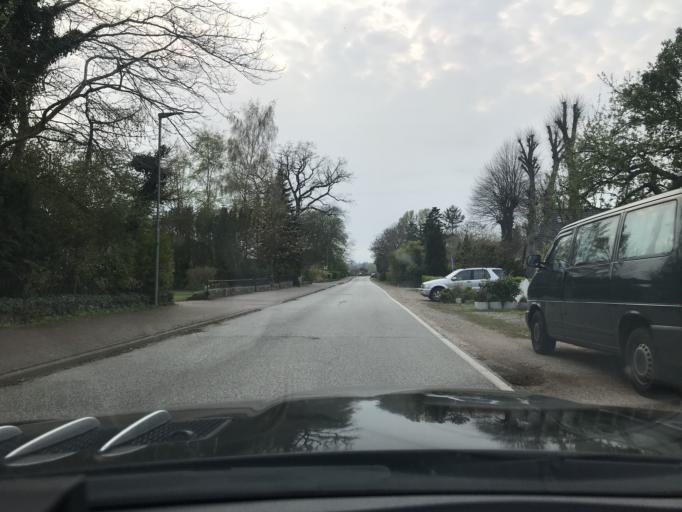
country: DE
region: Schleswig-Holstein
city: Burg auf Fehmarn
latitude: 54.4236
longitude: 11.2515
